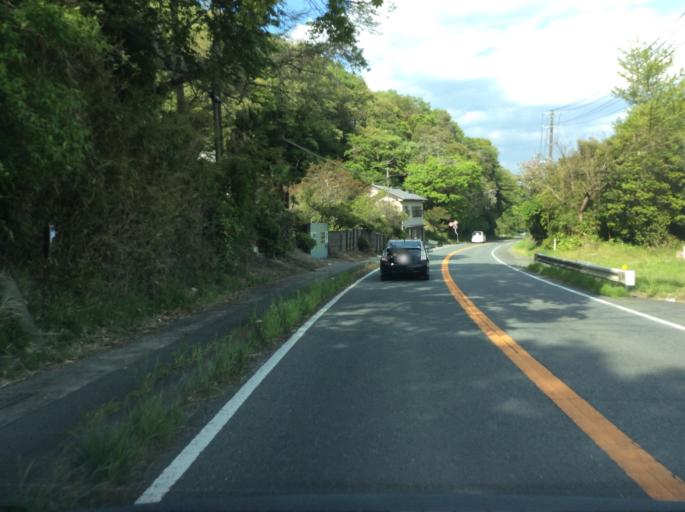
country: JP
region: Fukushima
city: Iwaki
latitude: 36.9348
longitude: 140.8304
